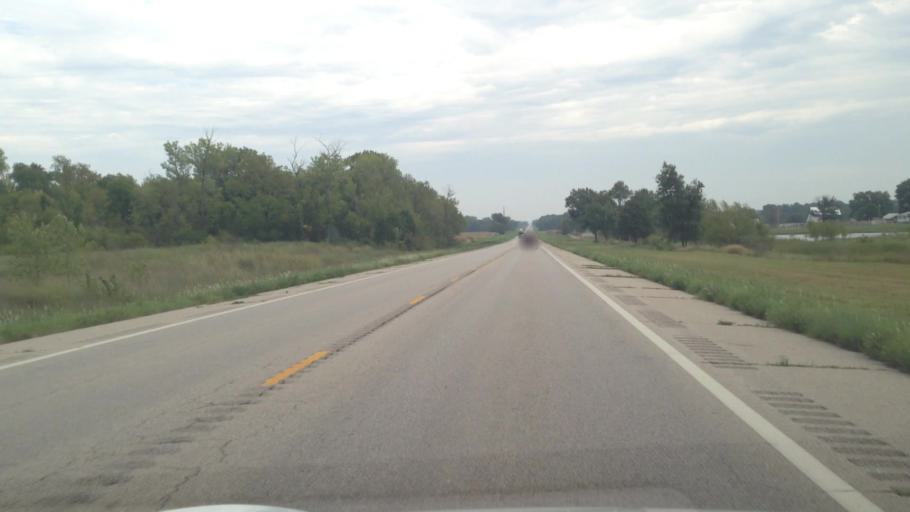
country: US
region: Kansas
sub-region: Crawford County
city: Pittsburg
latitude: 37.3392
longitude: -94.8002
